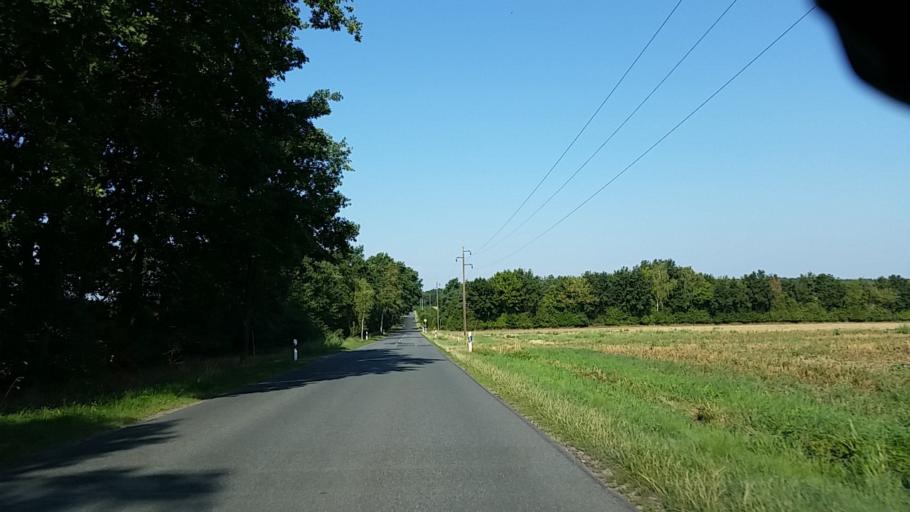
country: DE
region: Lower Saxony
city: Barwedel
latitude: 52.5256
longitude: 10.7670
